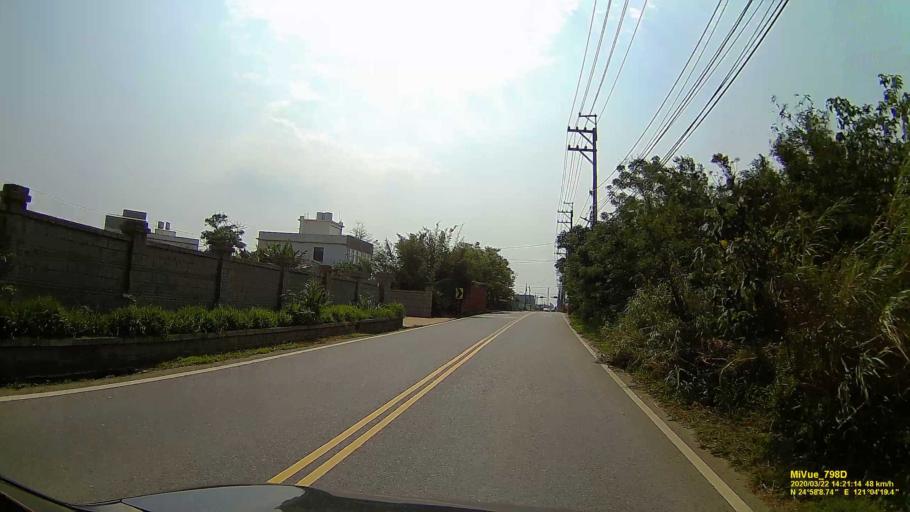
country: TW
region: Taiwan
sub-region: Hsinchu
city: Zhubei
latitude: 24.9691
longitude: 121.0717
